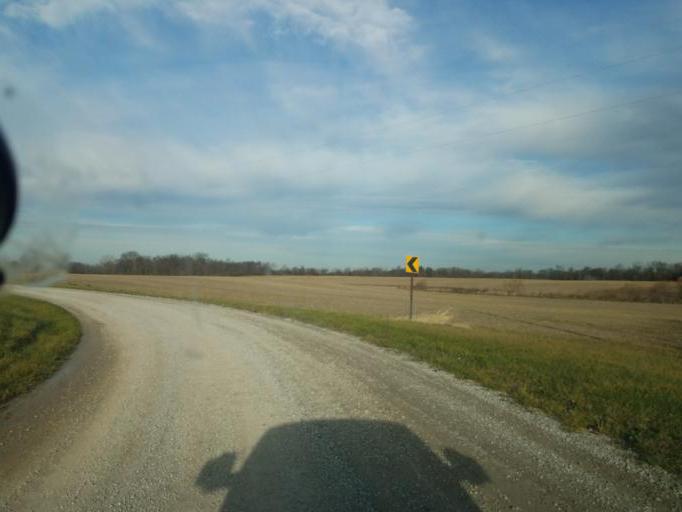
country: US
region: Ohio
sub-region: Morrow County
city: Mount Gilead
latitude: 40.5789
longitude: -82.8720
